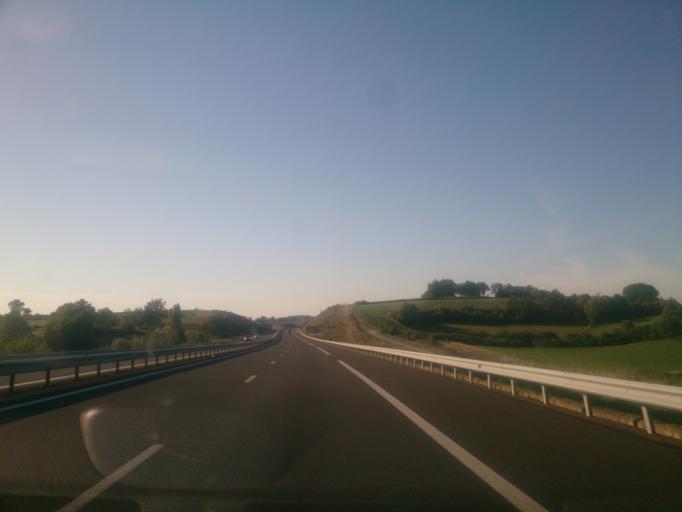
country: FR
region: Midi-Pyrenees
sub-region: Departement du Lot
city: Pradines
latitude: 44.5943
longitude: 1.5116
